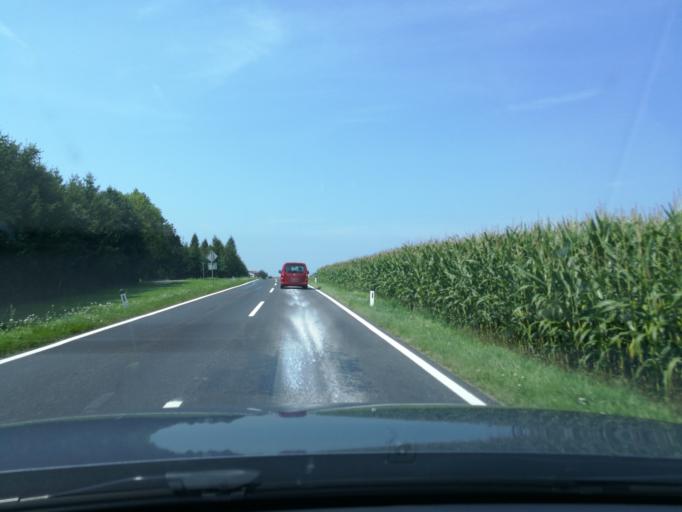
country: AT
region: Upper Austria
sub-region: Politischer Bezirk Grieskirchen
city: Grieskirchen
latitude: 48.3542
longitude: 13.7081
